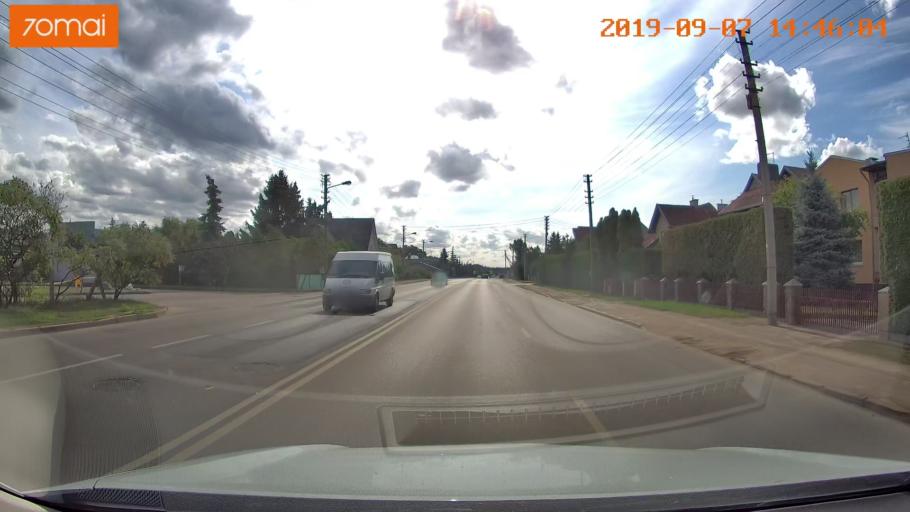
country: LT
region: Kauno apskritis
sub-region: Kaunas
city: Silainiai
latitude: 54.9285
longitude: 23.9067
